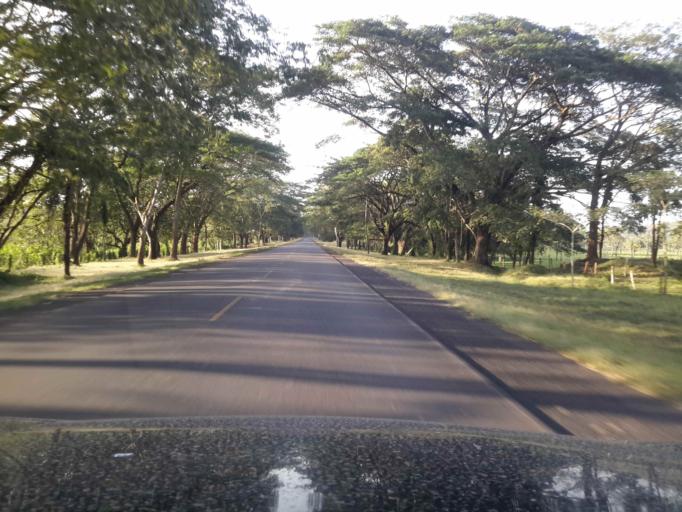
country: NI
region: Rio San Juan
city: San Miguelito
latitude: 11.4219
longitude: -84.8460
